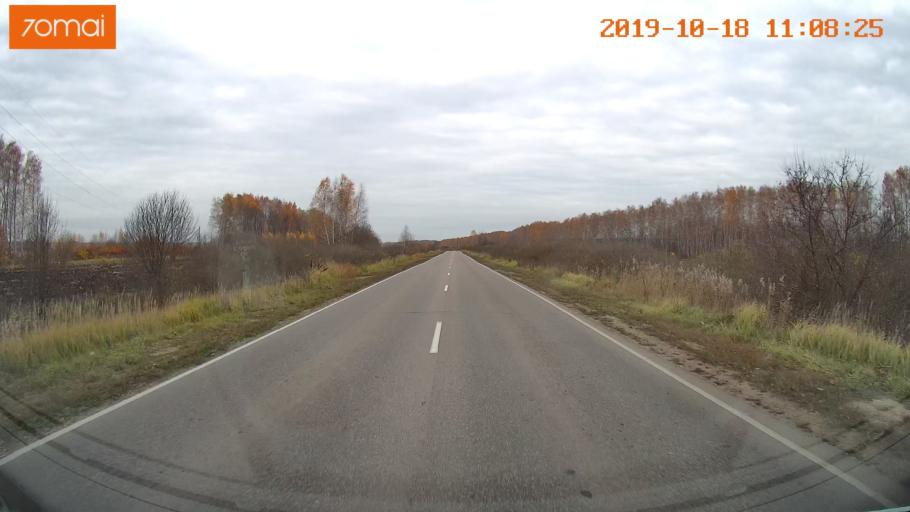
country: RU
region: Tula
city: Kimovsk
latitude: 53.9378
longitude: 38.5373
